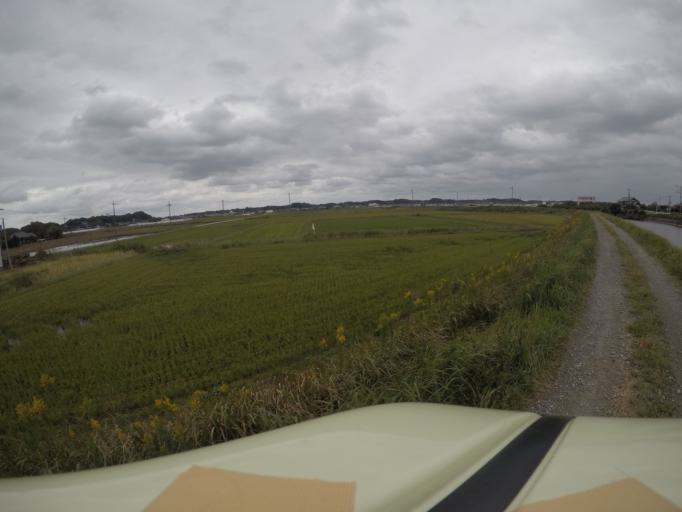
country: JP
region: Ibaraki
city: Ishioka
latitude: 36.1004
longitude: 140.4018
